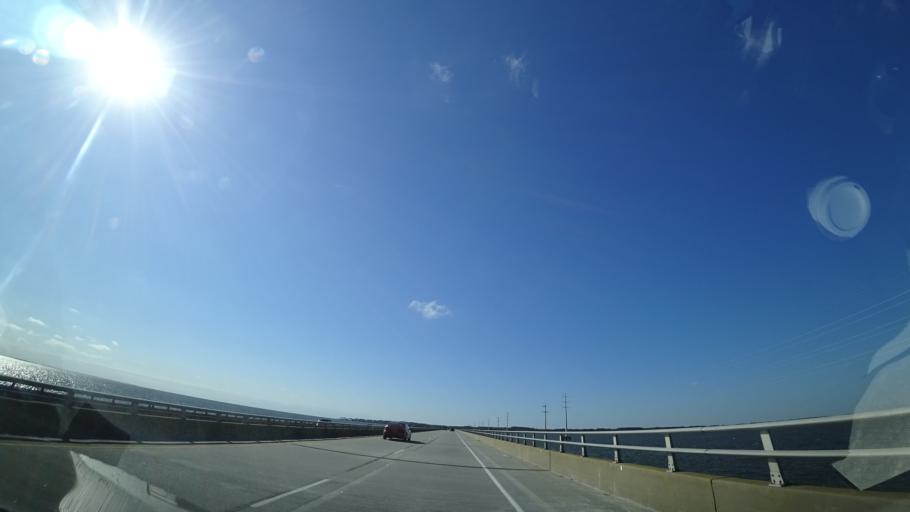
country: US
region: North Carolina
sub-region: Dare County
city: Southern Shores
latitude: 36.0864
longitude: -75.7683
